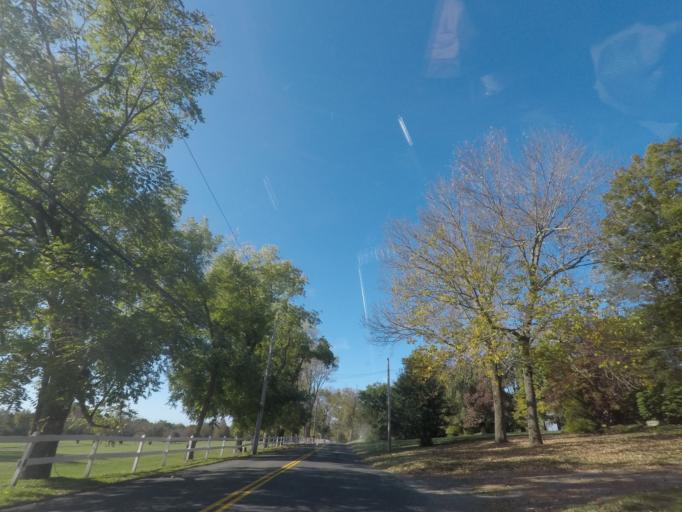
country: US
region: Connecticut
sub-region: Windham County
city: Thompson
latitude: 41.9847
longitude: -71.8275
